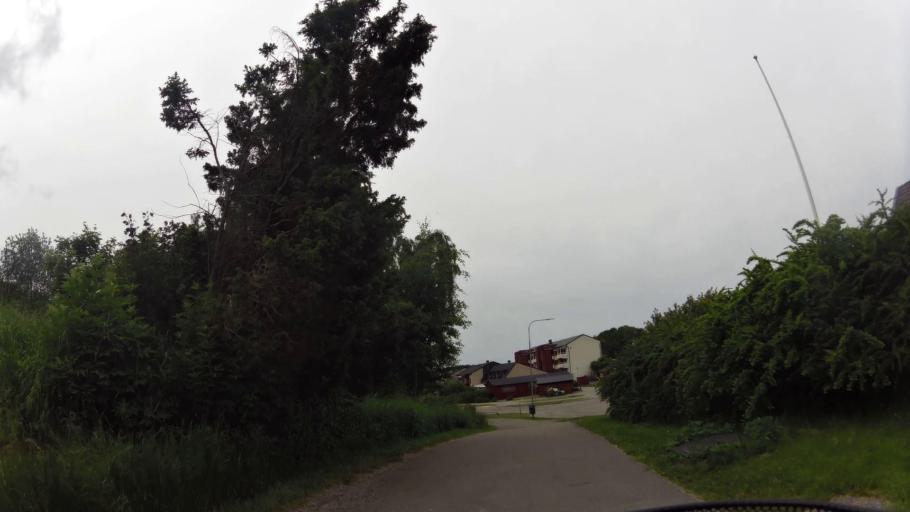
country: SE
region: OEstergoetland
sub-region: Linkopings Kommun
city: Linkoping
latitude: 58.3861
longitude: 15.5736
